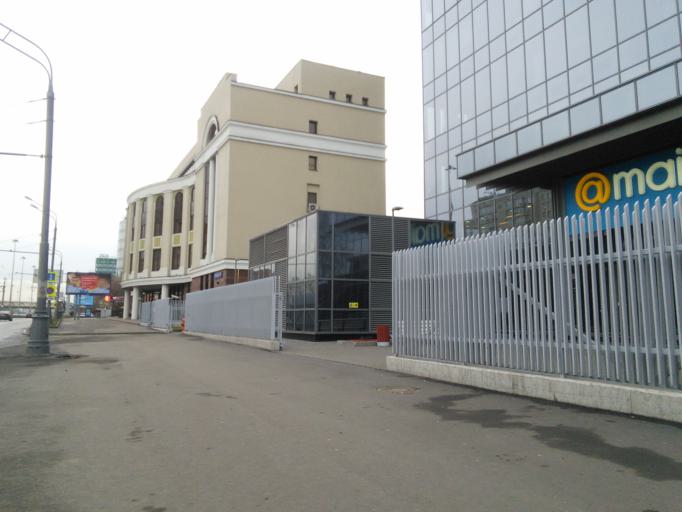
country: RU
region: Moscow
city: Sokol
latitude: 55.7973
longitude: 37.5379
